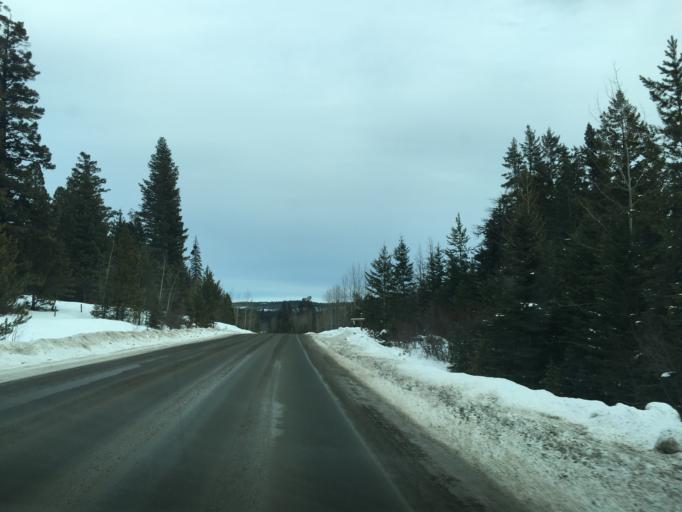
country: CA
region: British Columbia
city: Kamloops
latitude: 50.5262
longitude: -120.4625
